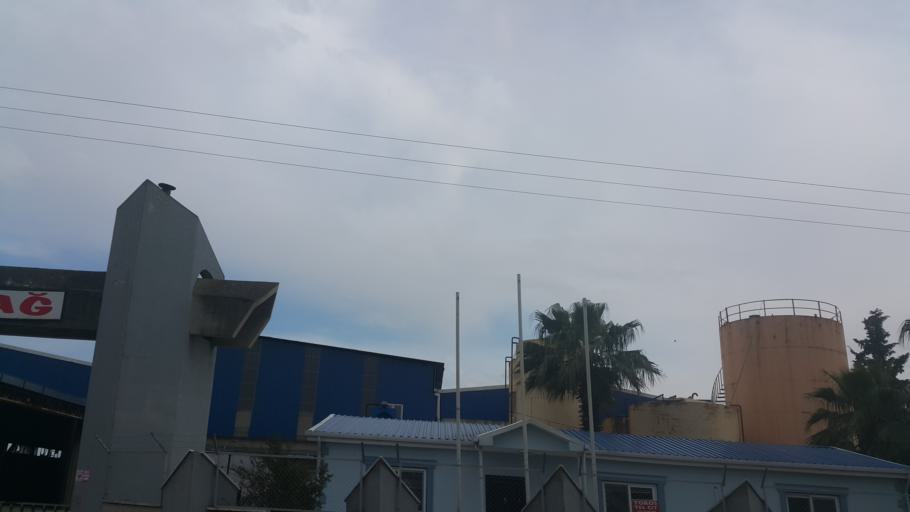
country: TR
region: Mersin
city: Yenice
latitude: 36.9808
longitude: 35.0968
